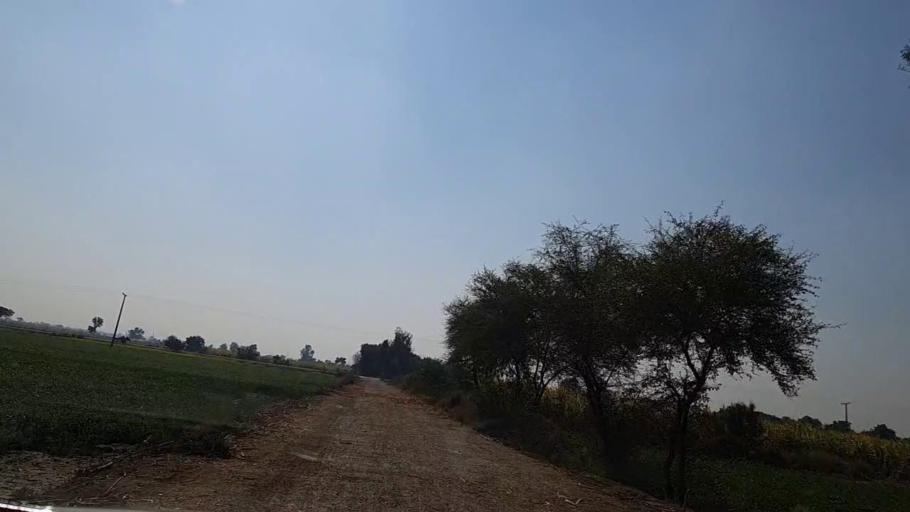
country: PK
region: Sindh
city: Sakrand
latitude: 26.2248
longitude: 68.3149
